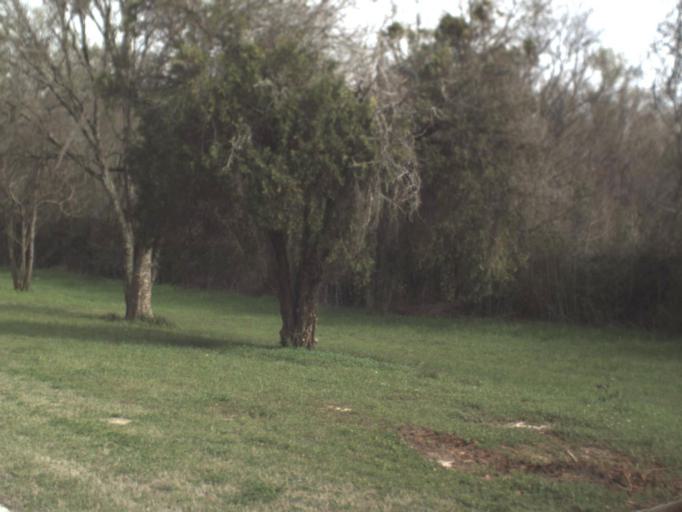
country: US
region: Florida
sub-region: Jefferson County
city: Monticello
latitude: 30.5257
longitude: -84.0116
